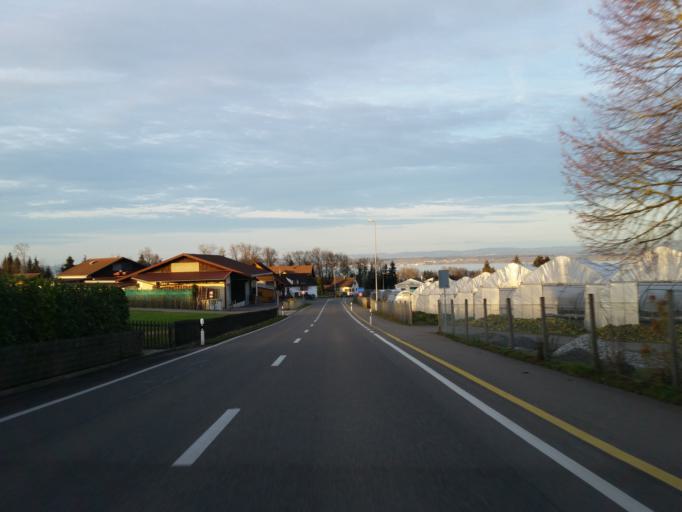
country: CH
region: Thurgau
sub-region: Arbon District
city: Uttwil
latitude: 47.5848
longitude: 9.3160
